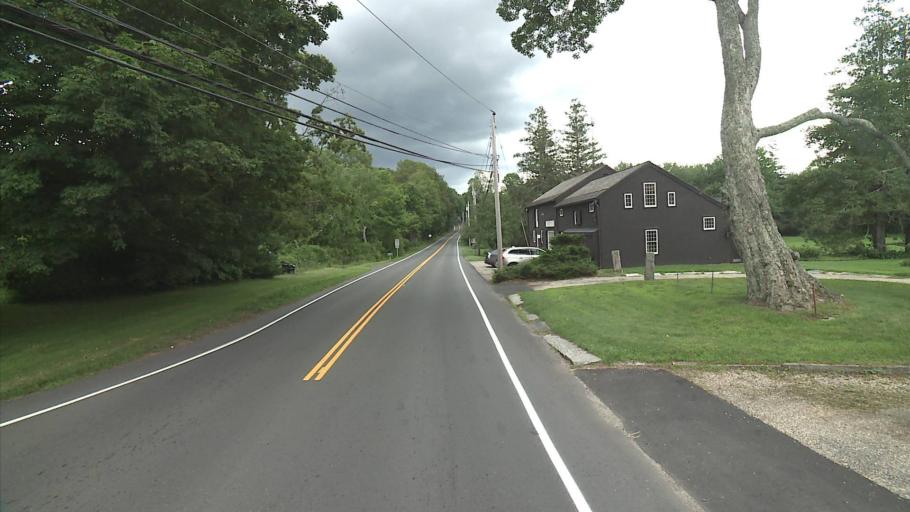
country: US
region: Connecticut
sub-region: Litchfield County
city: Woodbury
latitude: 41.5575
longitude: -73.3069
